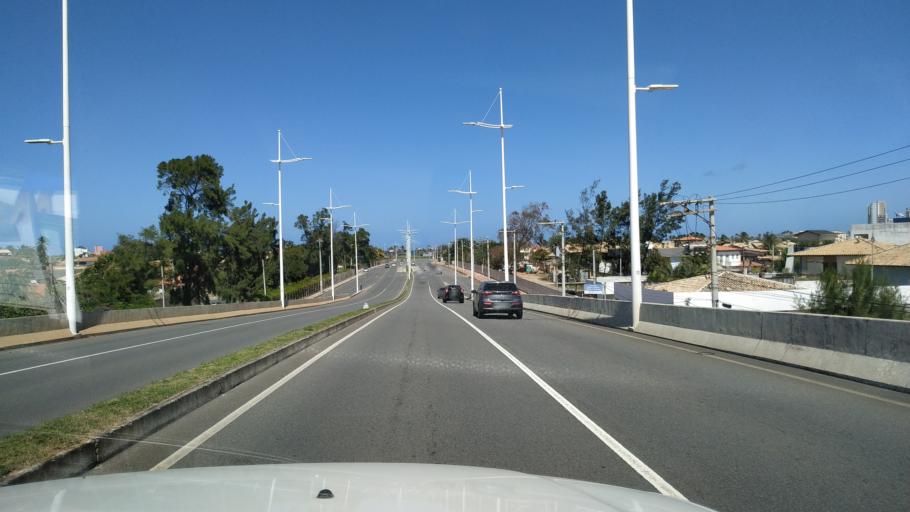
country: BR
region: Bahia
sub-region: Lauro De Freitas
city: Lauro de Freitas
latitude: -12.9491
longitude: -38.3846
